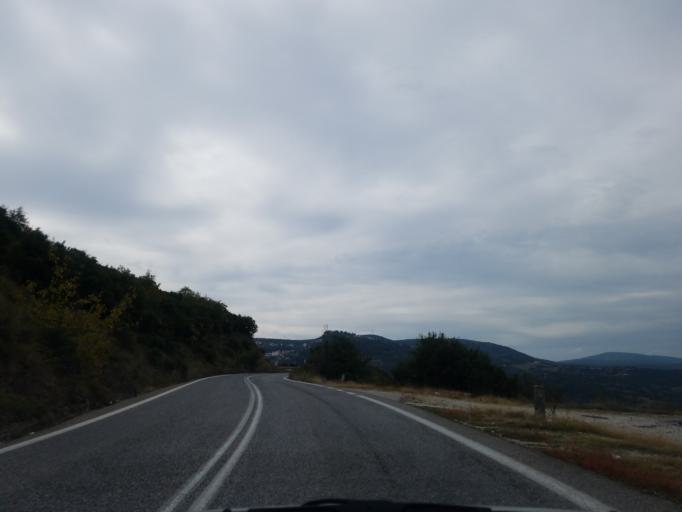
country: GR
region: Central Greece
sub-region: Nomos Fthiotidos
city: Domokos
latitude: 39.1431
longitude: 22.3086
